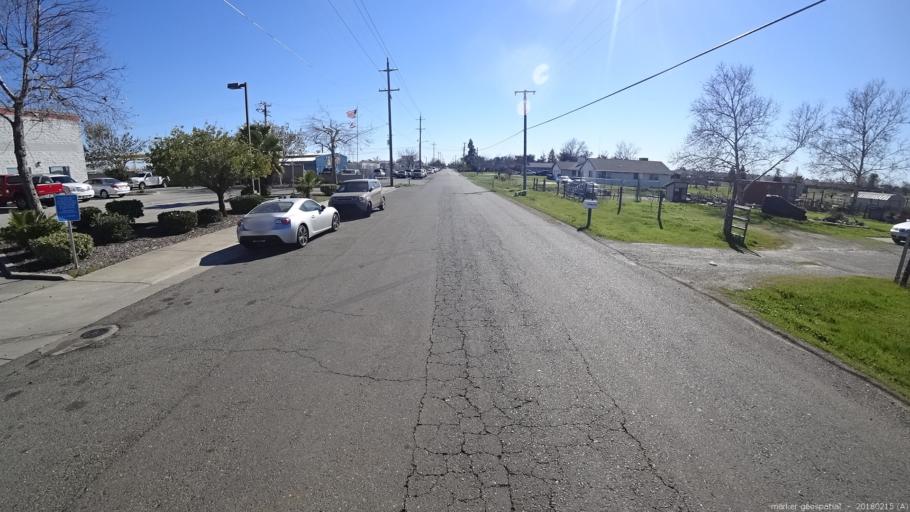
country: US
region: California
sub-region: Sacramento County
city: North Highlands
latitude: 38.6939
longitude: -121.3875
